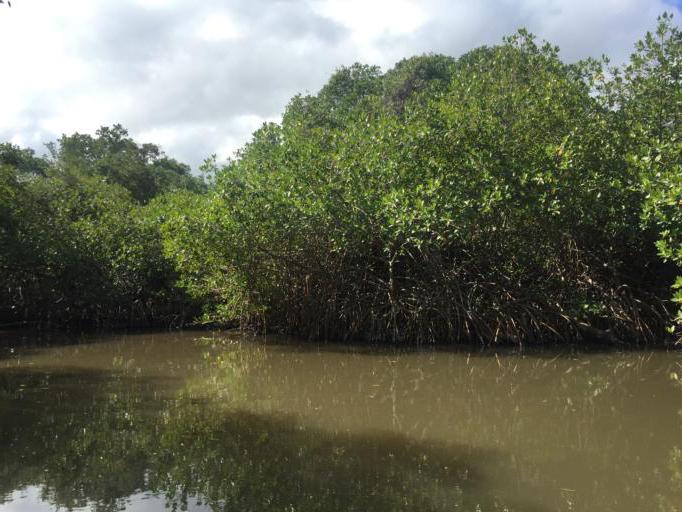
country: MX
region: Veracruz
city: Tecolutla
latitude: 20.4636
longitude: -97.0081
